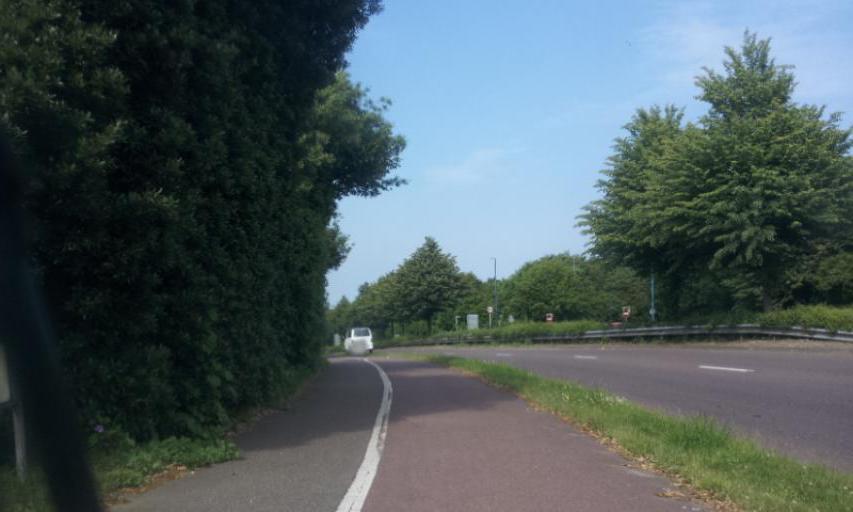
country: GB
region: England
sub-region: Kent
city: Gillingham
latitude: 51.3803
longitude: 0.5745
